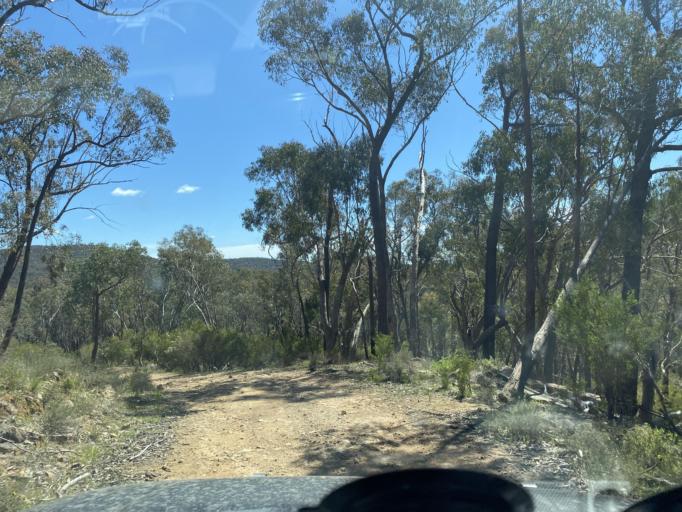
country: AU
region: Victoria
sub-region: Benalla
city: Benalla
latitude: -36.6978
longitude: 146.1516
